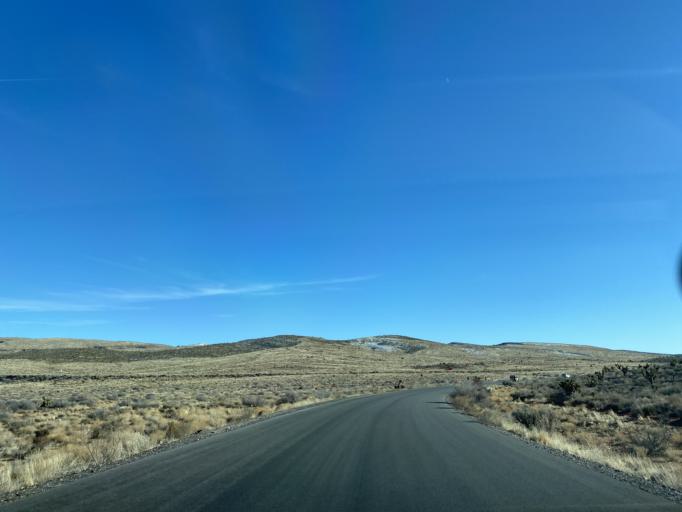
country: US
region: Nevada
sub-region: Clark County
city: Summerlin South
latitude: 36.1155
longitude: -115.4516
